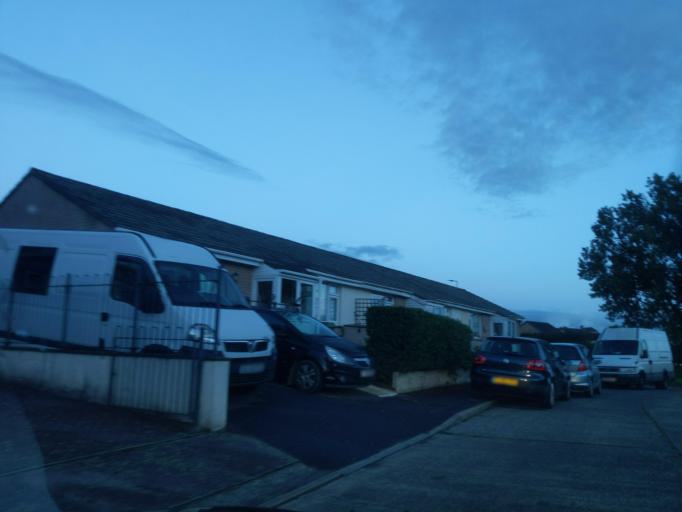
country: GB
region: England
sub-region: Devon
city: Great Torrington
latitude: 50.9587
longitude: -4.1307
